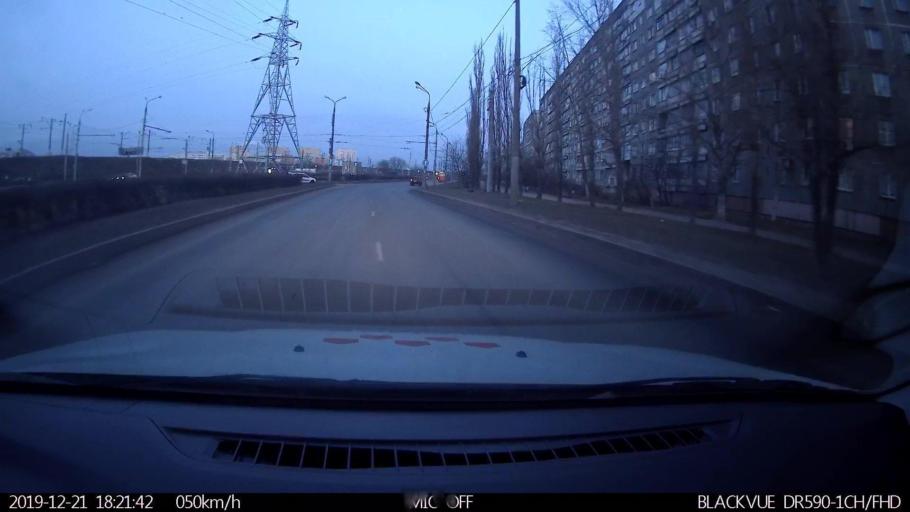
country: RU
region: Nizjnij Novgorod
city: Nizhniy Novgorod
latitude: 56.3371
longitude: 43.9263
